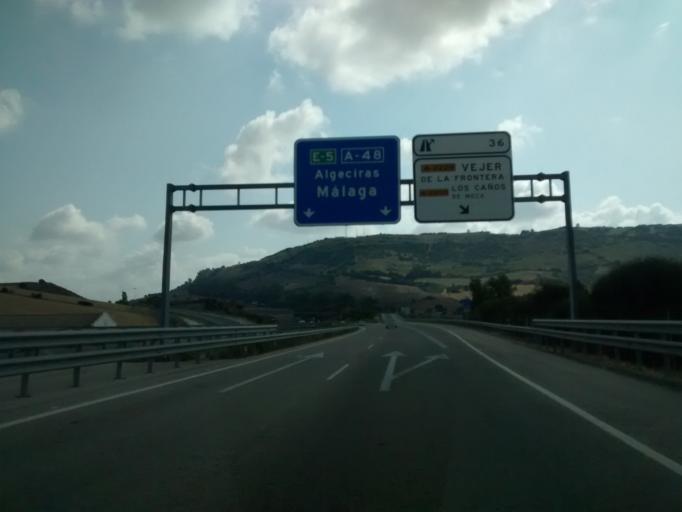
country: ES
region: Andalusia
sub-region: Provincia de Cadiz
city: Vejer de la Frontera
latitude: 36.2538
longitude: -5.9880
